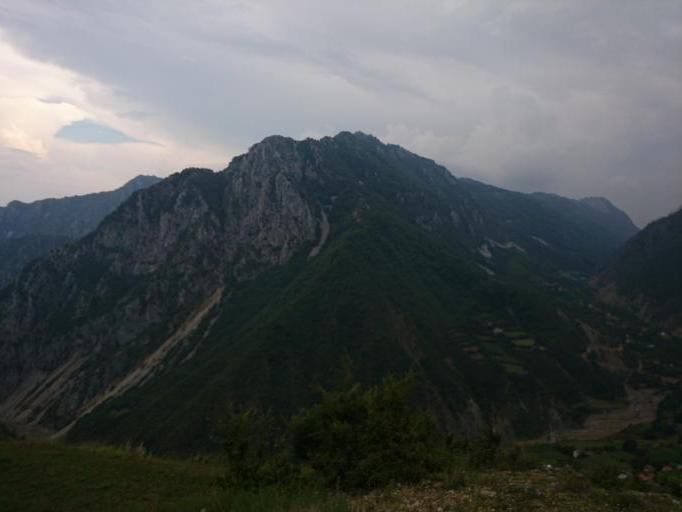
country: AL
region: Diber
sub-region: Rrethi i Dibres
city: Fushe-Lure
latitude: 41.7634
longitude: 20.2261
